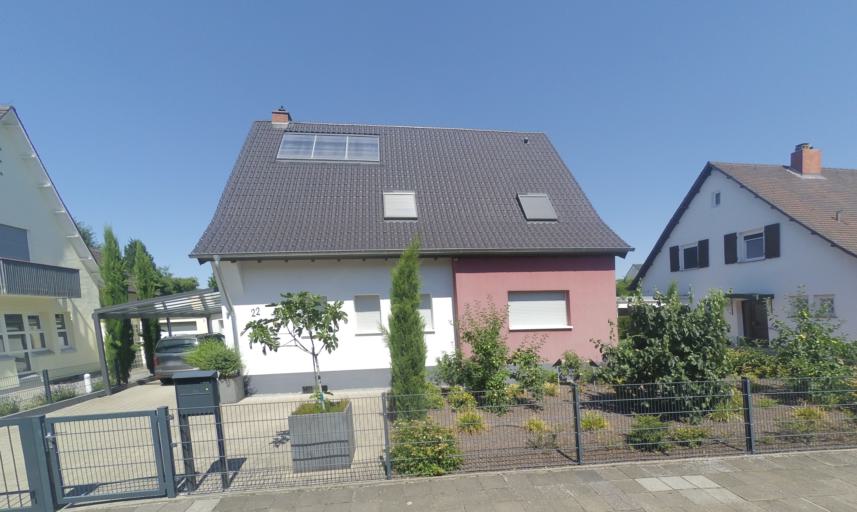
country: DE
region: Rheinland-Pfalz
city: Limburgerhof
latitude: 49.4191
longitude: 8.4001
